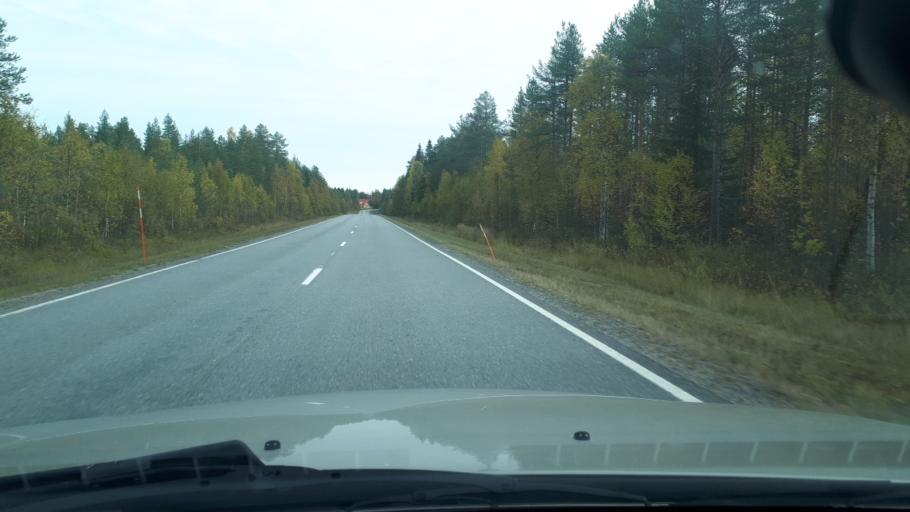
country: FI
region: Lapland
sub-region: Rovaniemi
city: Ranua
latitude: 66.0109
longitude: 26.3017
